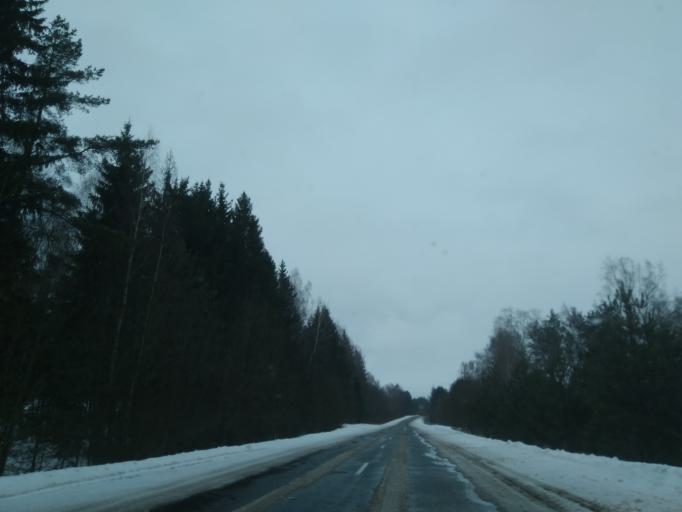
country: BY
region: Minsk
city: Ivyanyets
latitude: 53.8479
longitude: 26.7908
